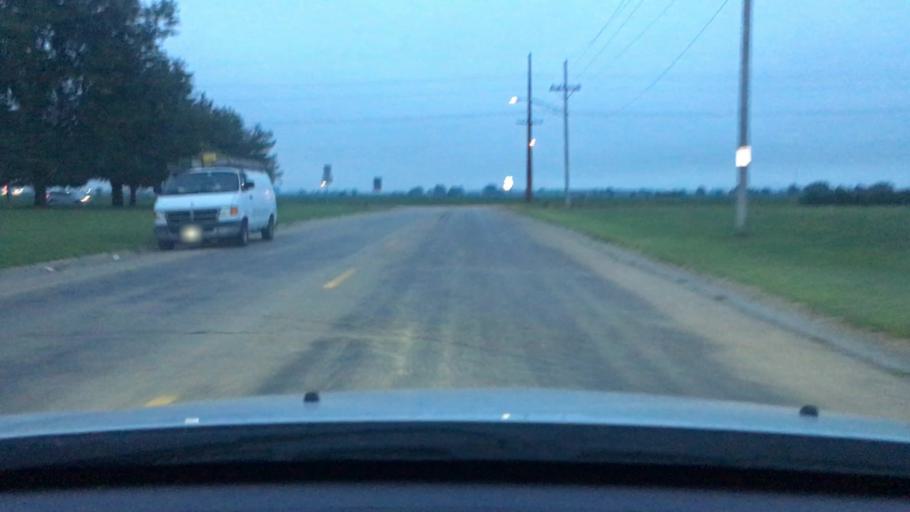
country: US
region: Illinois
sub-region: Ogle County
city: Rochelle
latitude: 41.9261
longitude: -89.0557
